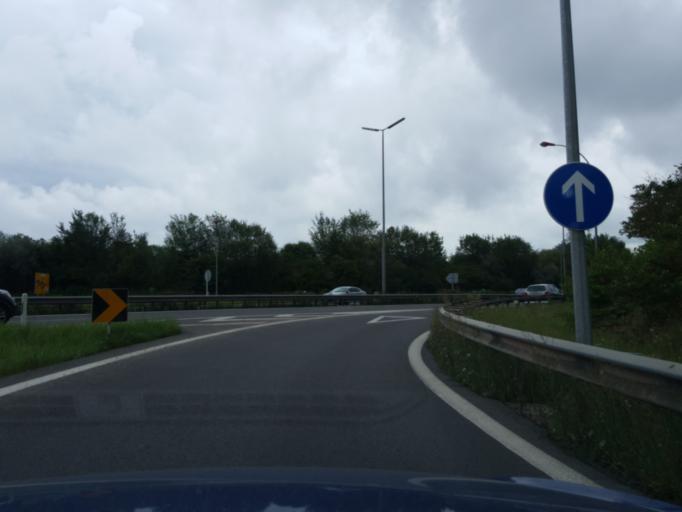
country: LU
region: Luxembourg
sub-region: Canton de Mersch
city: Mersch
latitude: 49.7608
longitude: 6.0913
